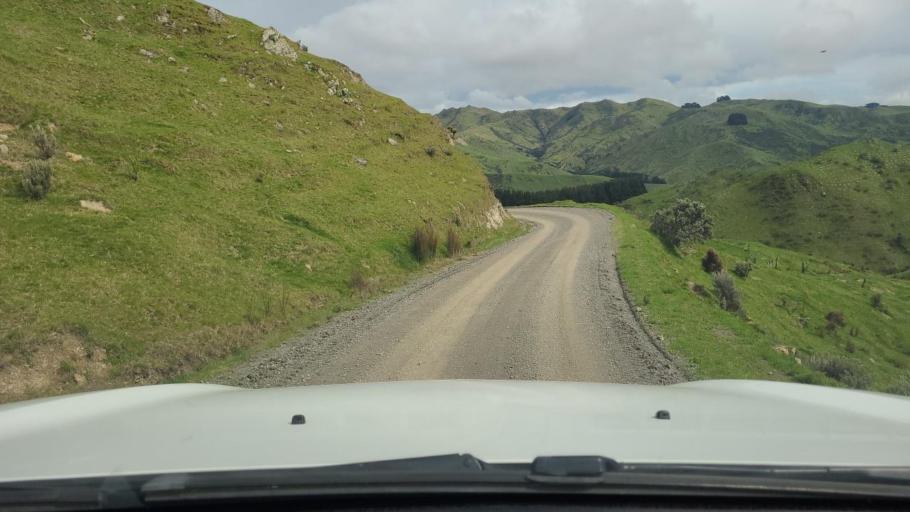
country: NZ
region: Wellington
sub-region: South Wairarapa District
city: Waipawa
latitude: -41.3896
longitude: 175.4644
